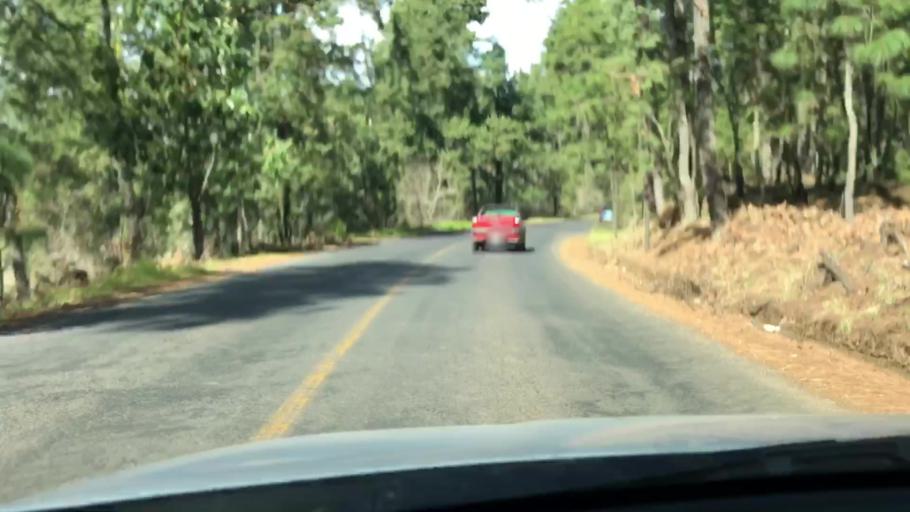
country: MX
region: Jalisco
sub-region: Amacueca
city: Tepec
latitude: 20.0869
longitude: -103.7157
